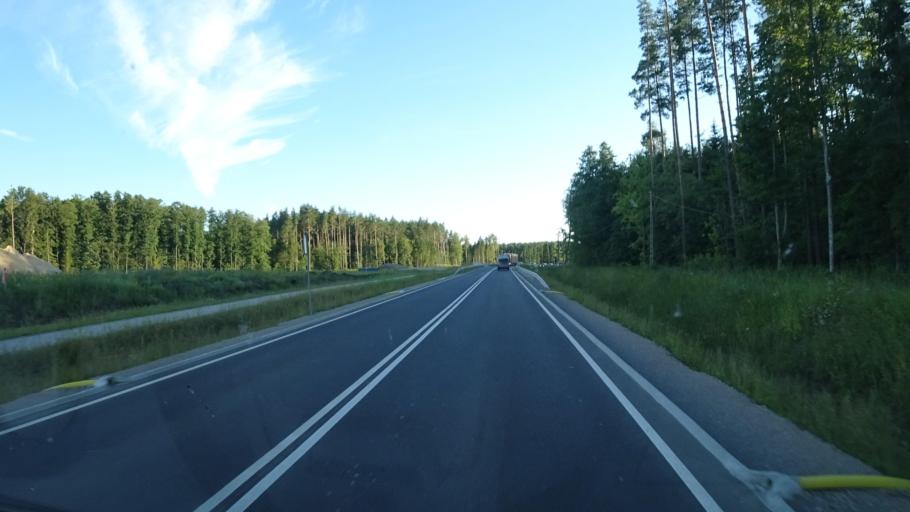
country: PL
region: Warmian-Masurian Voivodeship
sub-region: Powiat elcki
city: Elk
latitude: 53.8468
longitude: 22.4560
